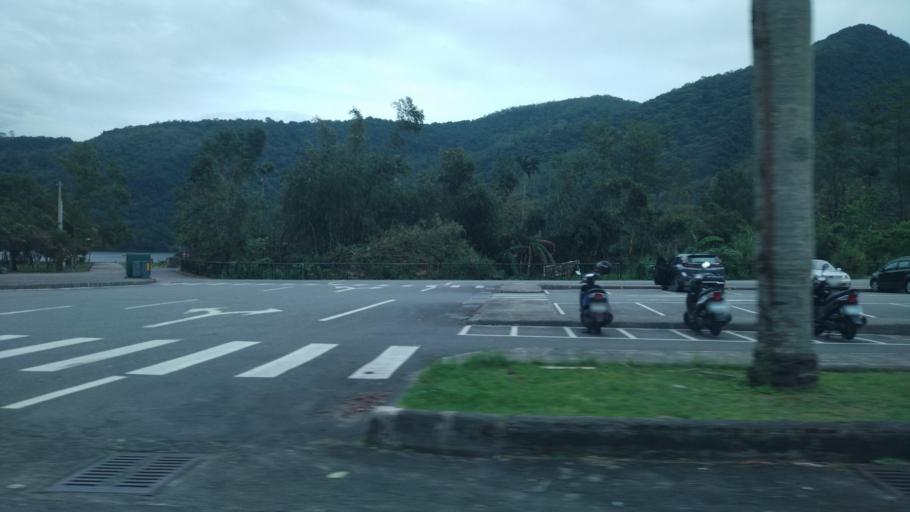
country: TW
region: Taiwan
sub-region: Hualien
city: Hualian
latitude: 23.9247
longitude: 121.5057
